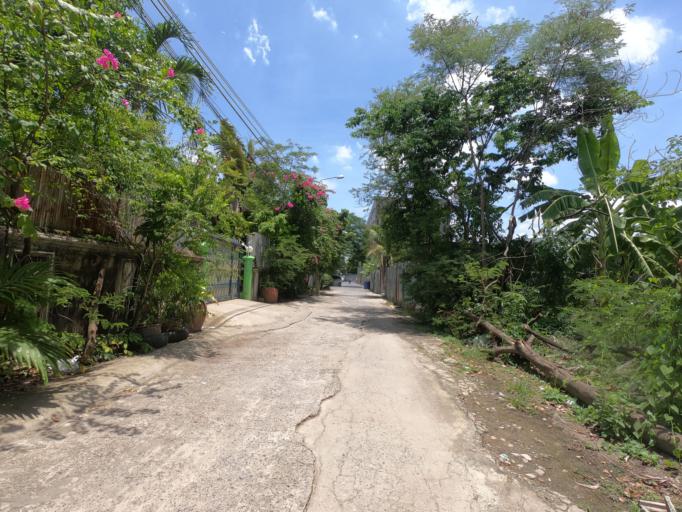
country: TH
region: Bangkok
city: Lat Phrao
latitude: 13.8257
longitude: 100.6237
